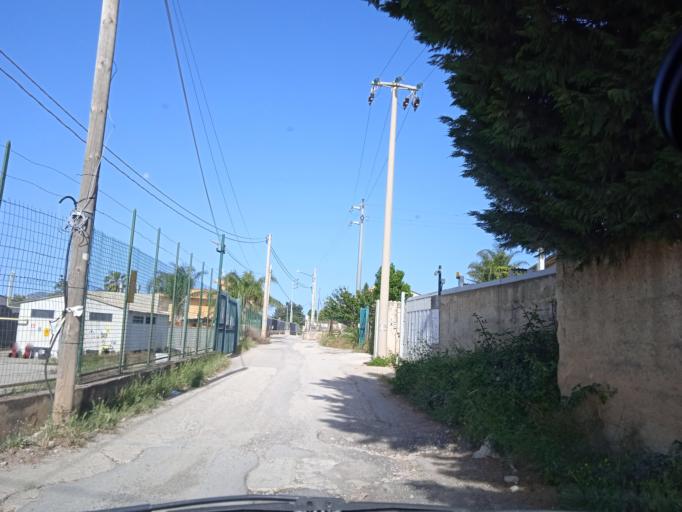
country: IT
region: Sicily
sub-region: Palermo
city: Portella di Mare
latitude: 38.0807
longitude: 13.4542
